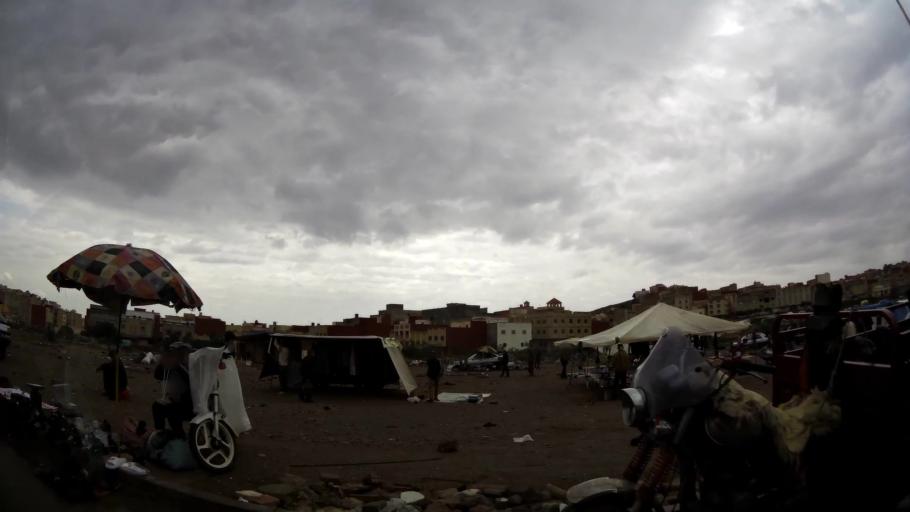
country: MA
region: Oriental
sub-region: Nador
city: Nador
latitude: 35.1505
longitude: -3.0045
